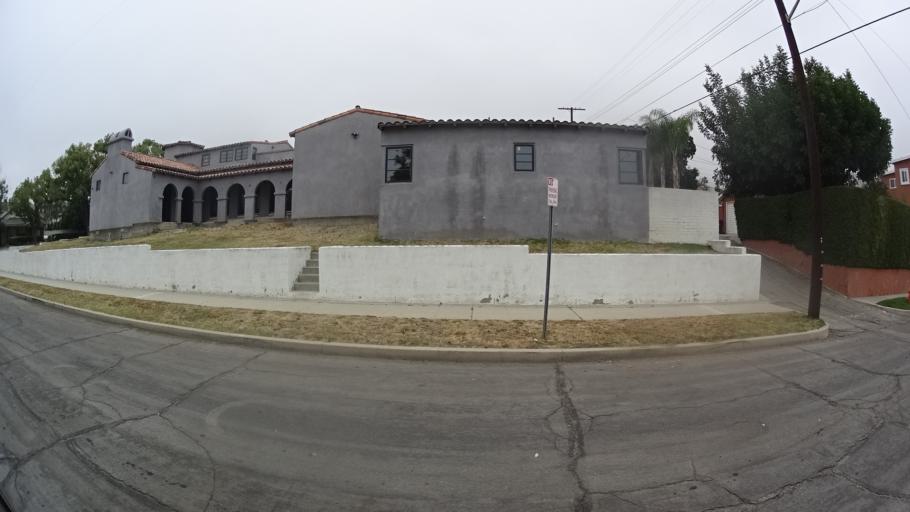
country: US
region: California
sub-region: Los Angeles County
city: Burbank
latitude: 34.1879
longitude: -118.2988
